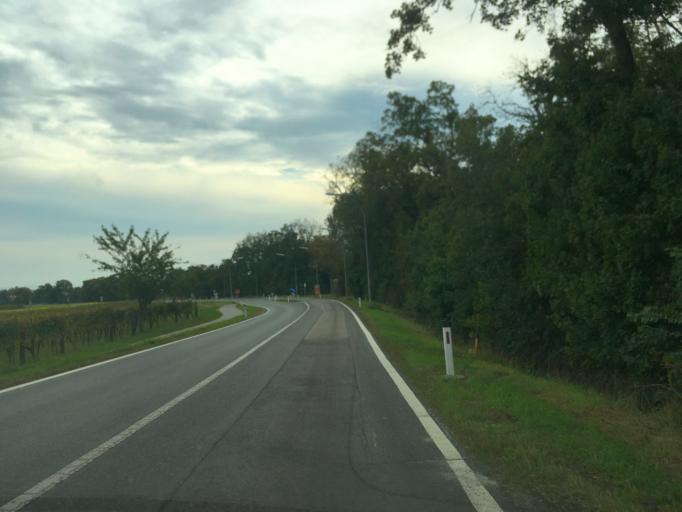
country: AT
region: Burgenland
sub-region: Politischer Bezirk Neusiedl am See
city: Winden am See
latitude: 47.9547
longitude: 16.7393
